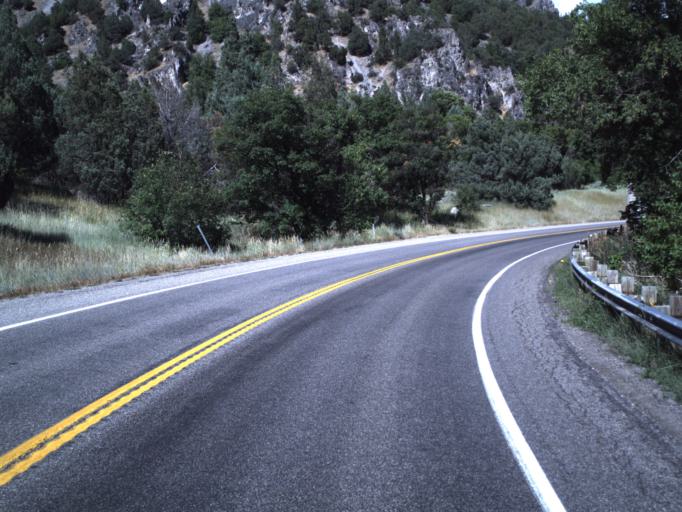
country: US
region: Utah
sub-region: Cache County
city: North Logan
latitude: 41.7730
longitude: -111.6580
